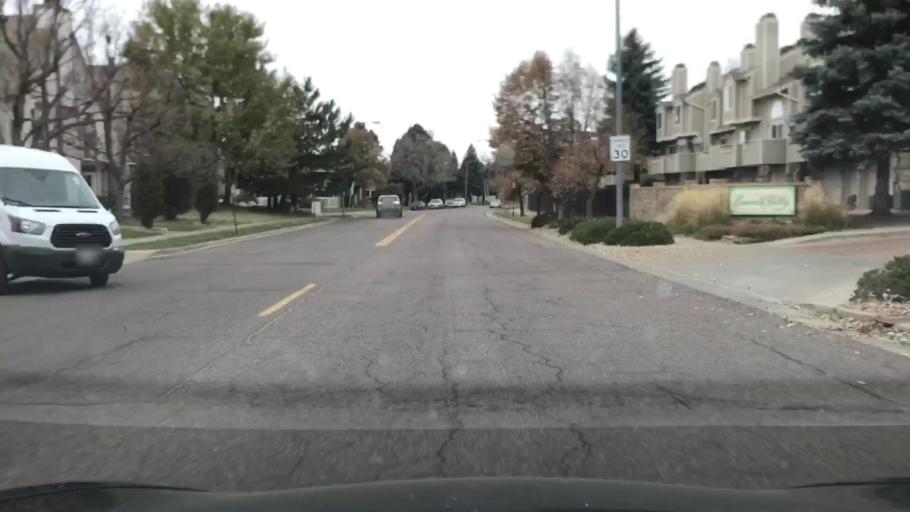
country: US
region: Colorado
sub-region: Arapahoe County
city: Glendale
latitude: 39.6842
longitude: -104.8916
